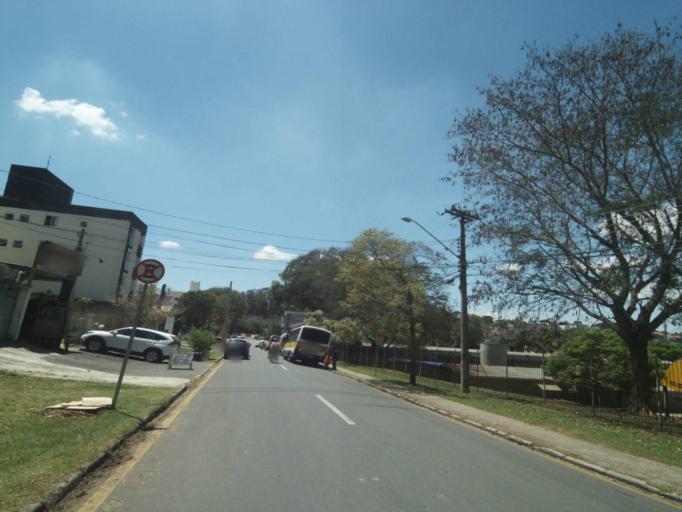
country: BR
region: Parana
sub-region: Curitiba
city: Curitiba
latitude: -25.3888
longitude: -49.2267
